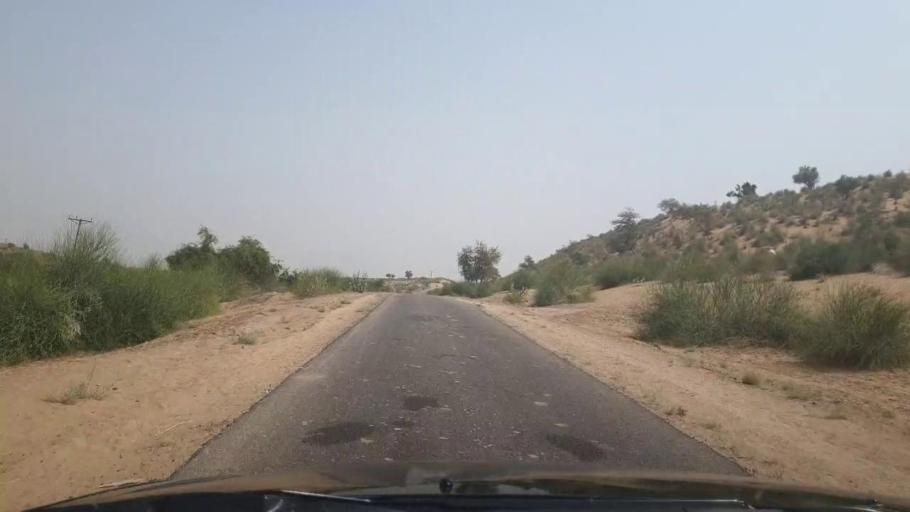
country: PK
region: Sindh
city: Islamkot
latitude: 24.9463
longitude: 70.4181
